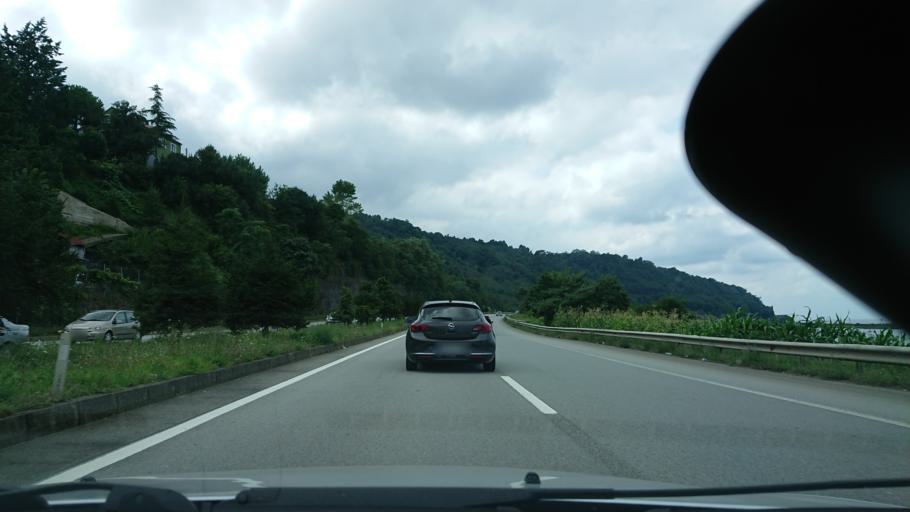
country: TR
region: Giresun
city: Eynesil
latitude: 41.0734
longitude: 39.1840
